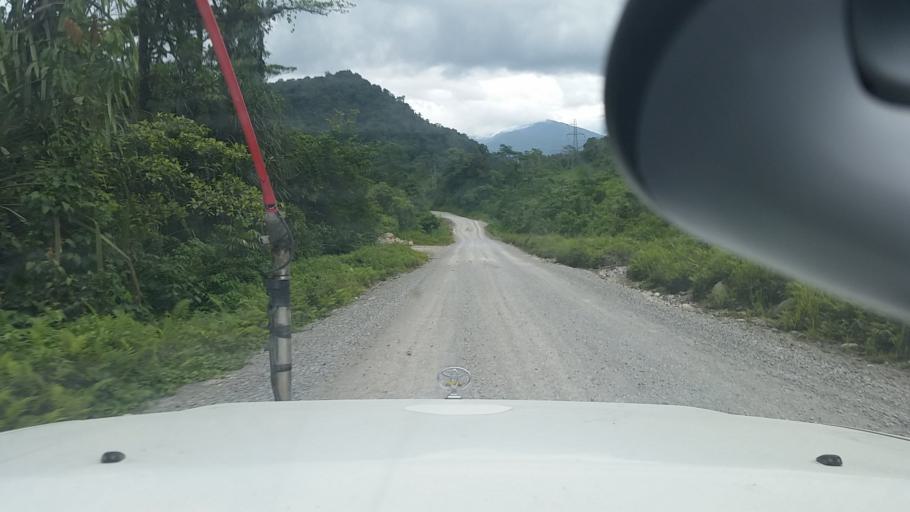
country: ID
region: Papua
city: Mindiptana
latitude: -5.3231
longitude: 141.2581
